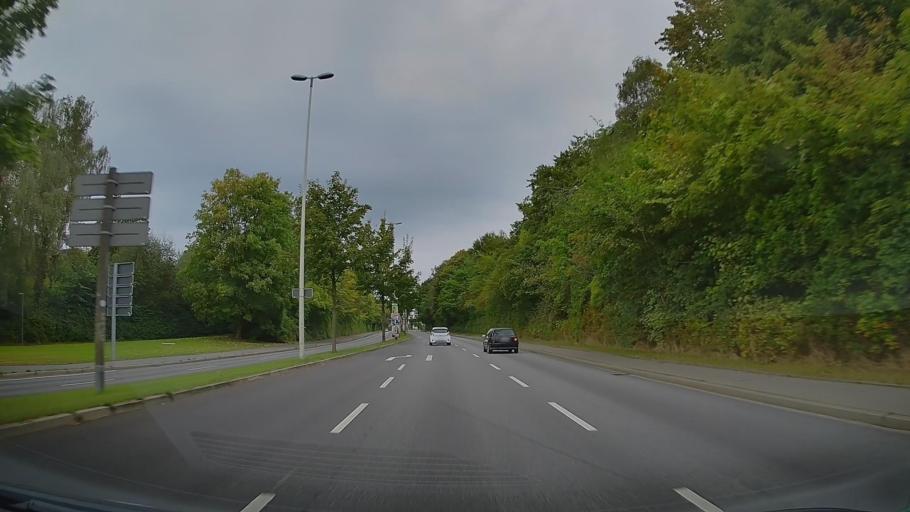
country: DE
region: Schleswig-Holstein
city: Monkeberg
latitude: 54.3295
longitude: 10.1908
